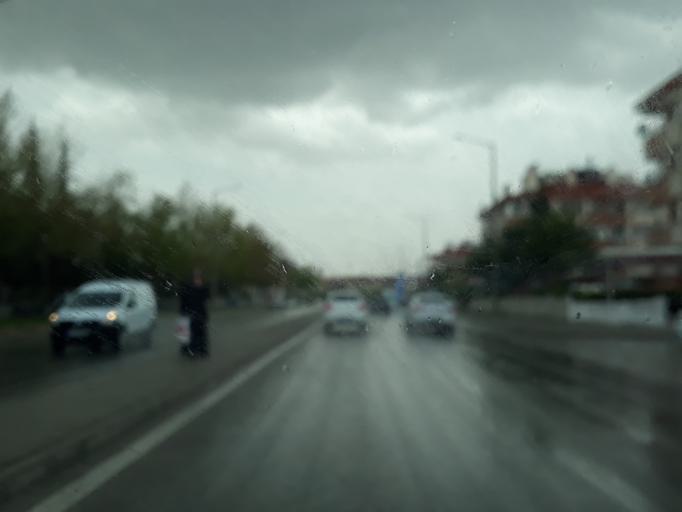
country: TR
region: Konya
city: Selcuklu
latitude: 37.9183
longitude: 32.4926
